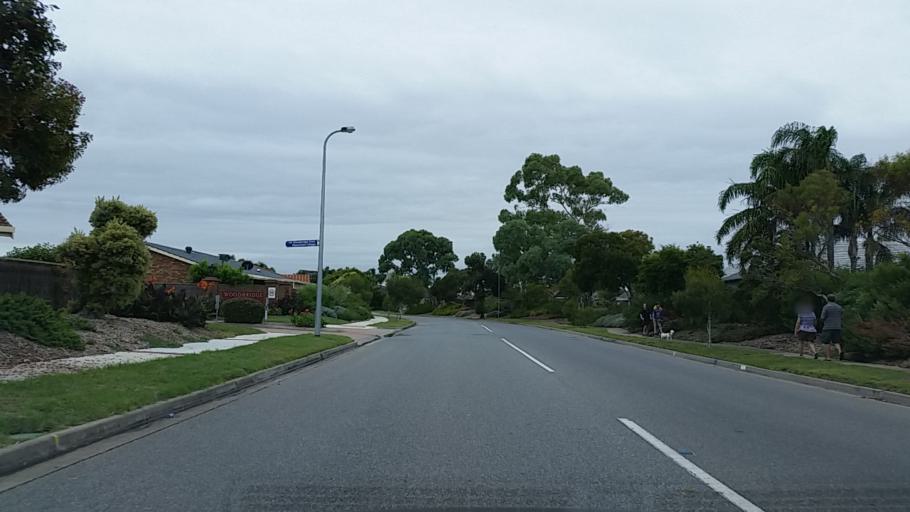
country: AU
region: South Australia
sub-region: Charles Sturt
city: West Lakes Shore
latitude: -34.8632
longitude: 138.4955
